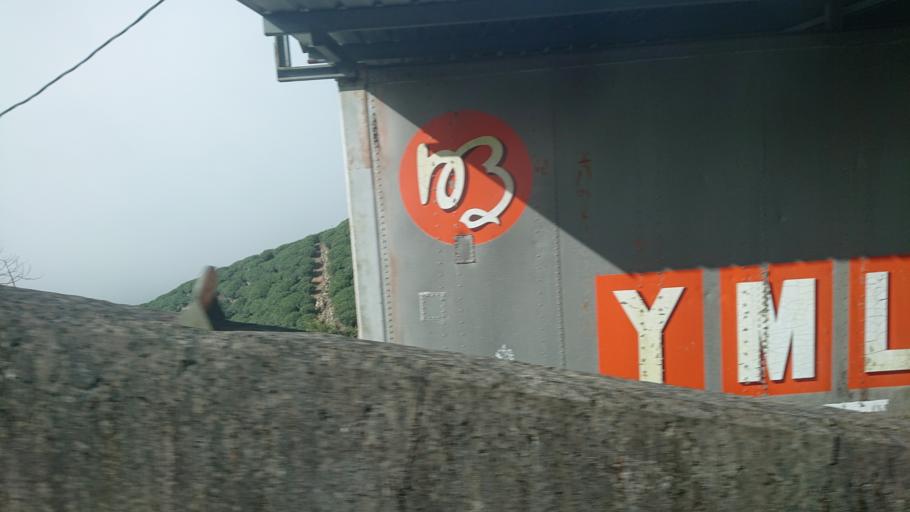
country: TW
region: Taiwan
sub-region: Chiayi
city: Jiayi Shi
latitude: 23.4759
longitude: 120.6982
